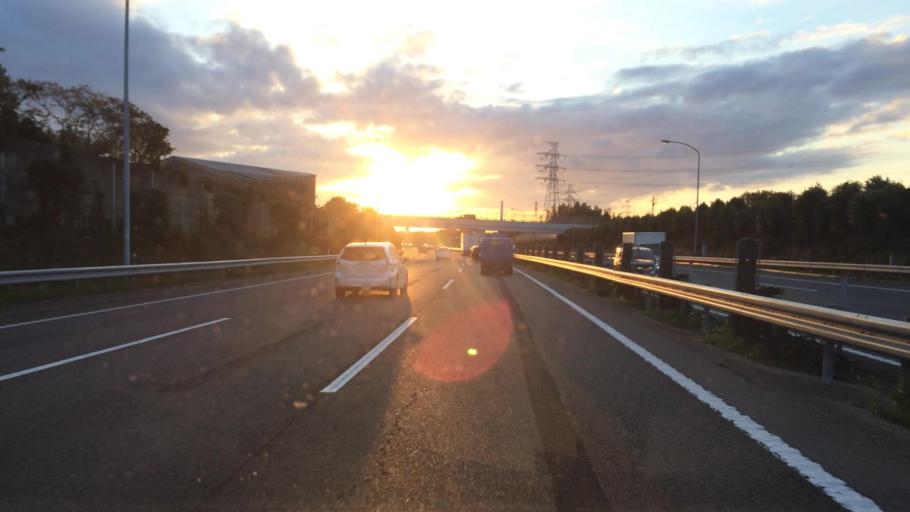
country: JP
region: Chiba
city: Yotsukaido
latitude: 35.6803
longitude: 140.1418
